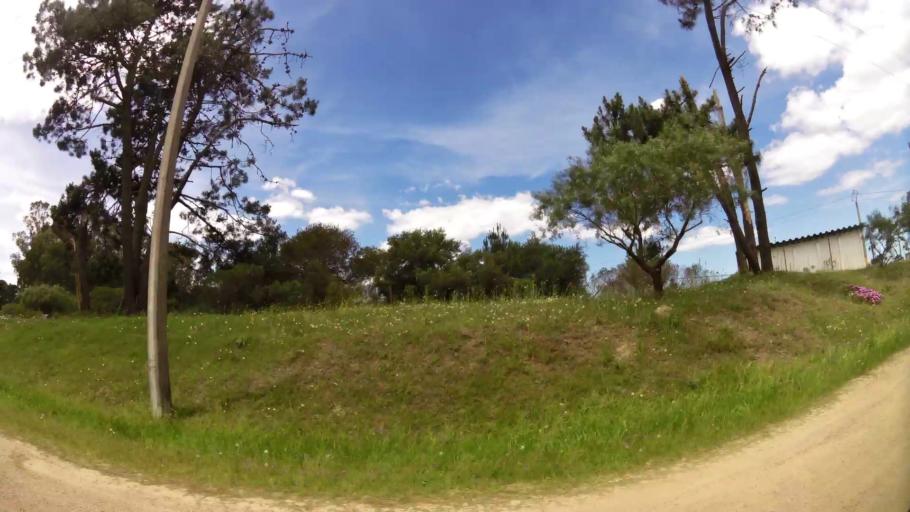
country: UY
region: Canelones
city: Pando
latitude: -34.8103
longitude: -55.9389
